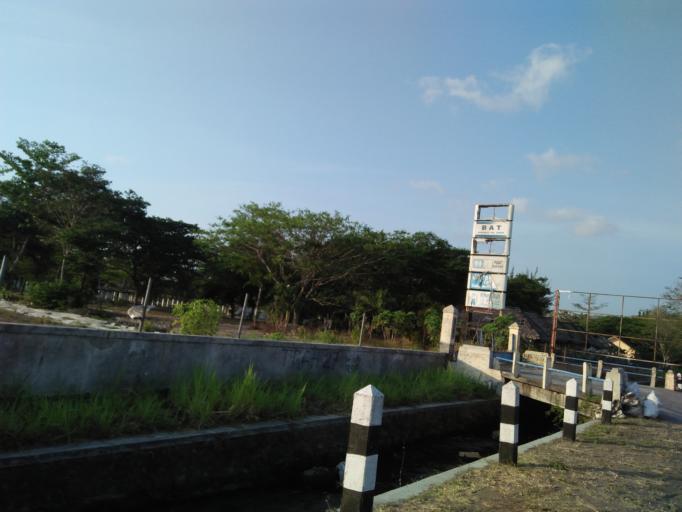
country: ID
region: Daerah Istimewa Yogyakarta
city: Pundong
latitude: -7.9434
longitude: 110.3322
